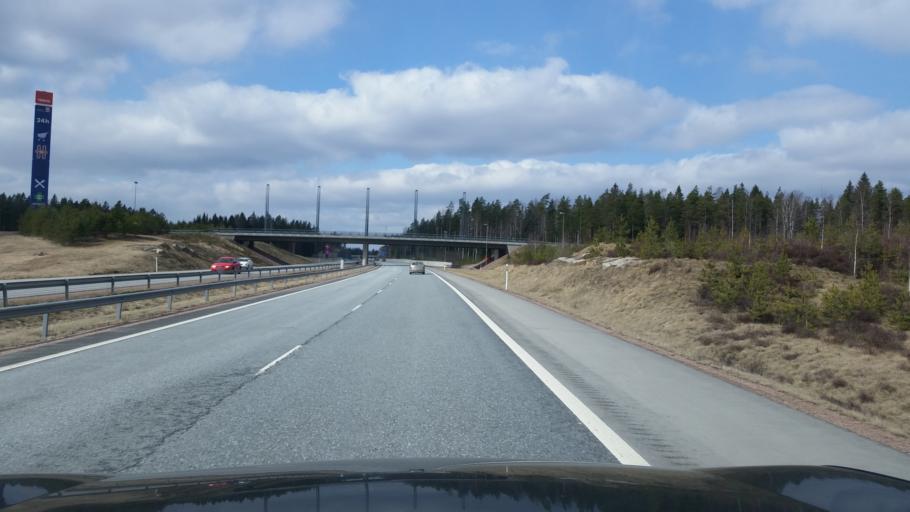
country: FI
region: Varsinais-Suomi
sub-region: Salo
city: Suomusjaervi
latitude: 60.3813
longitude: 23.6210
